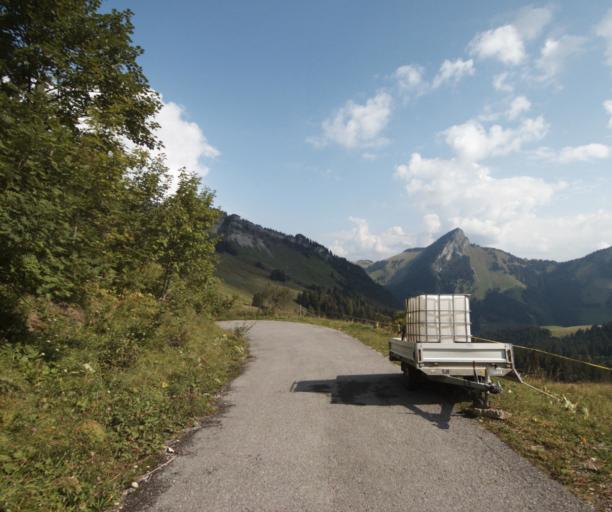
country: CH
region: Vaud
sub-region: Riviera-Pays-d'Enhaut District
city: Caux
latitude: 46.4247
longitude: 7.0017
